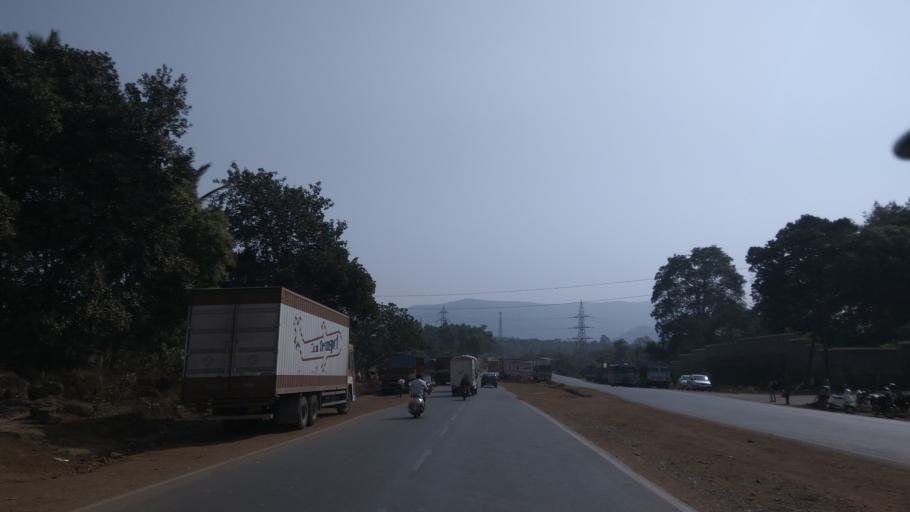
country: IN
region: Goa
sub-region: North Goa
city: Palle
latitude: 15.4163
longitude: 74.0700
